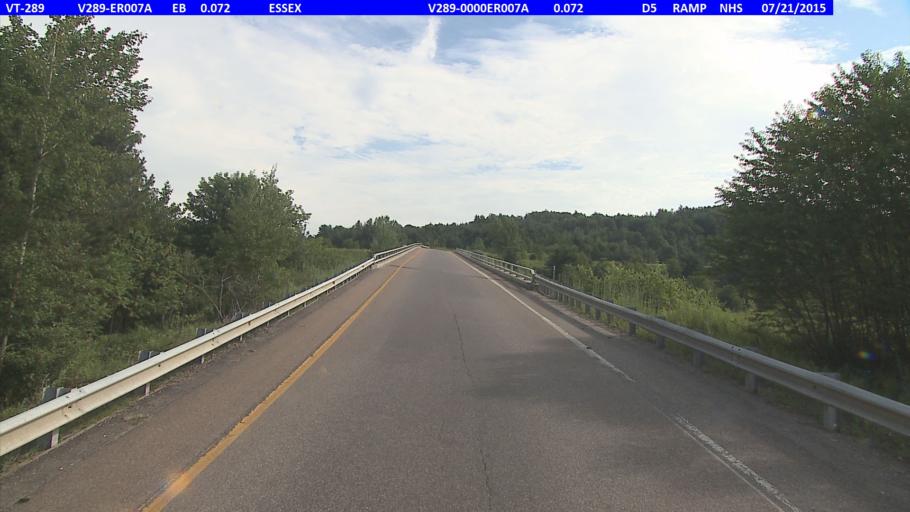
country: US
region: Vermont
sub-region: Chittenden County
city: Essex Junction
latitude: 44.5160
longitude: -73.1215
